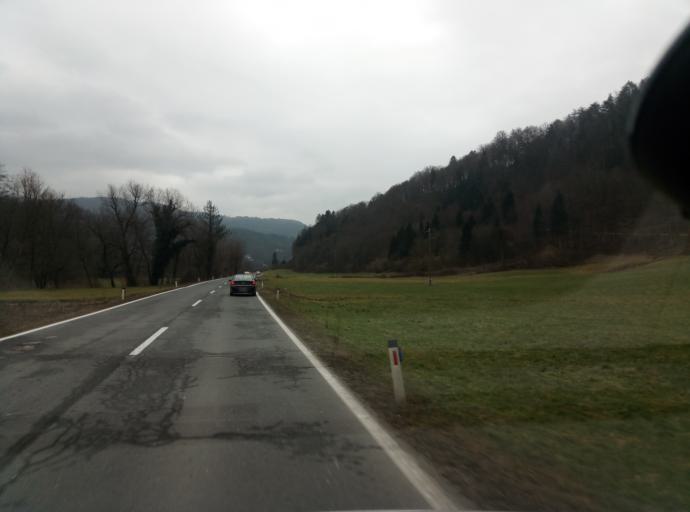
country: SI
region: Smartno pri Litiji
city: Smartno pri Litiji
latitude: 46.0780
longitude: 14.8725
